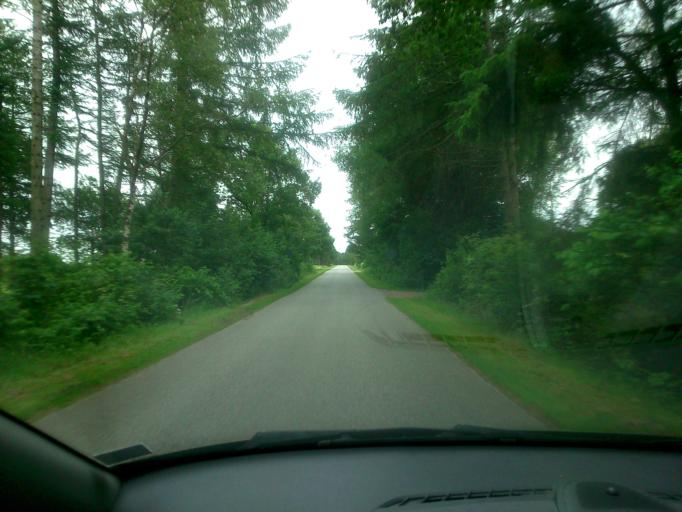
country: DK
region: Central Jutland
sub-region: Ringkobing-Skjern Kommune
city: Skjern
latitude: 55.9991
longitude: 8.4660
